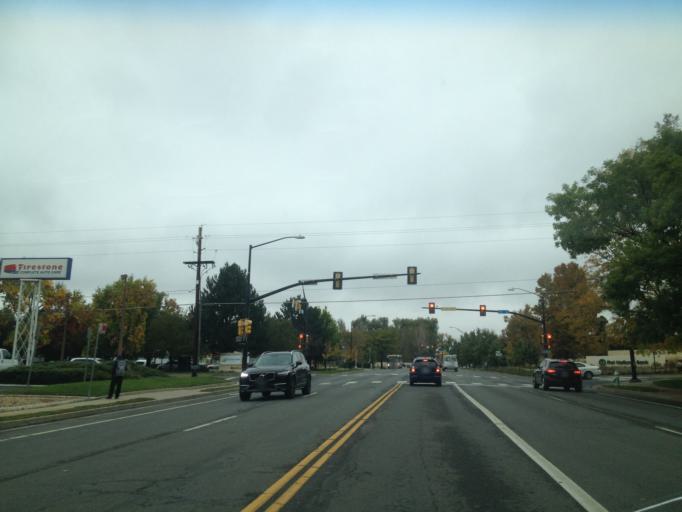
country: US
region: Colorado
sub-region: Boulder County
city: Boulder
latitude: 40.0360
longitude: -105.2537
